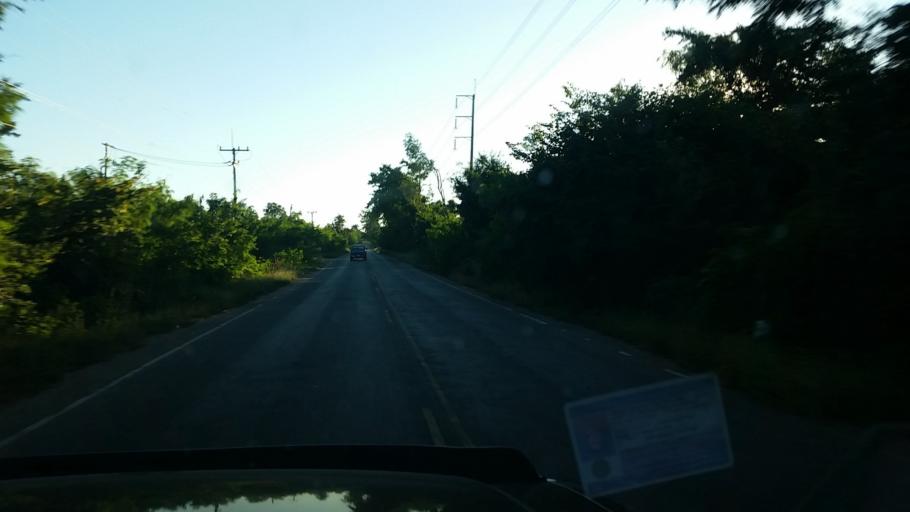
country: TH
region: Chaiyaphum
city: Nong Bua Rawe
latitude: 15.6877
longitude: 101.7042
